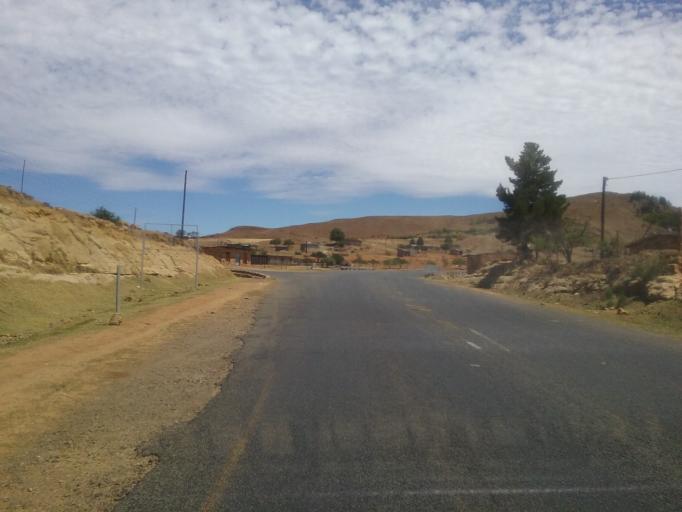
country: LS
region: Mafeteng
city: Mafeteng
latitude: -29.9192
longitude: 27.2497
